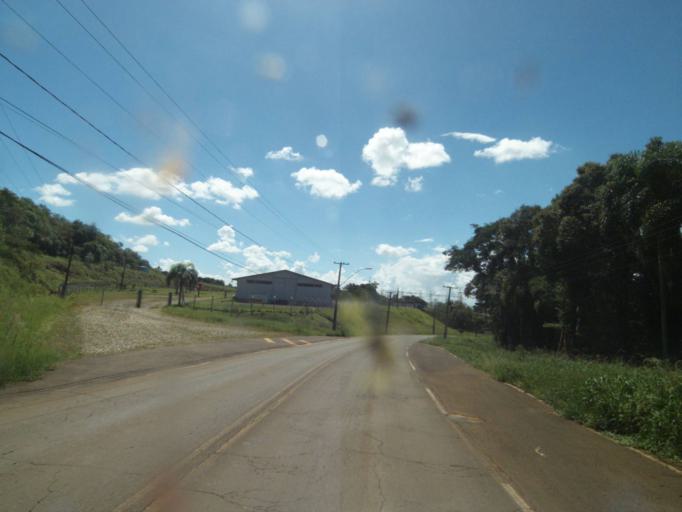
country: BR
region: Parana
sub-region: Chopinzinho
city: Chopinzinho
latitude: -25.7907
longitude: -52.0933
